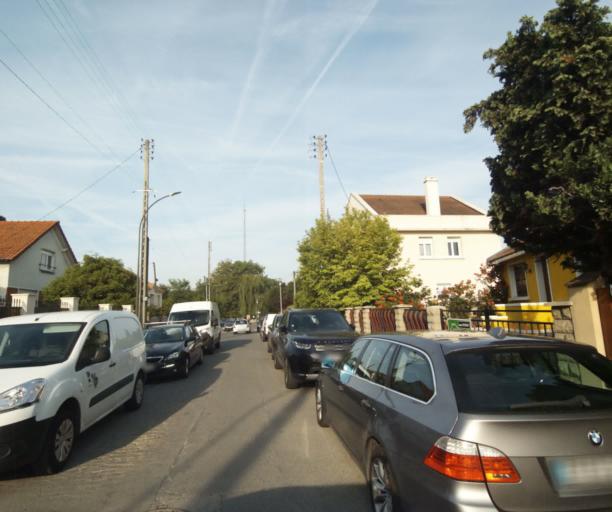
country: FR
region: Ile-de-France
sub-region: Departement du Val-d'Oise
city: Saint-Gratien
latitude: 48.9540
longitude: 2.2812
